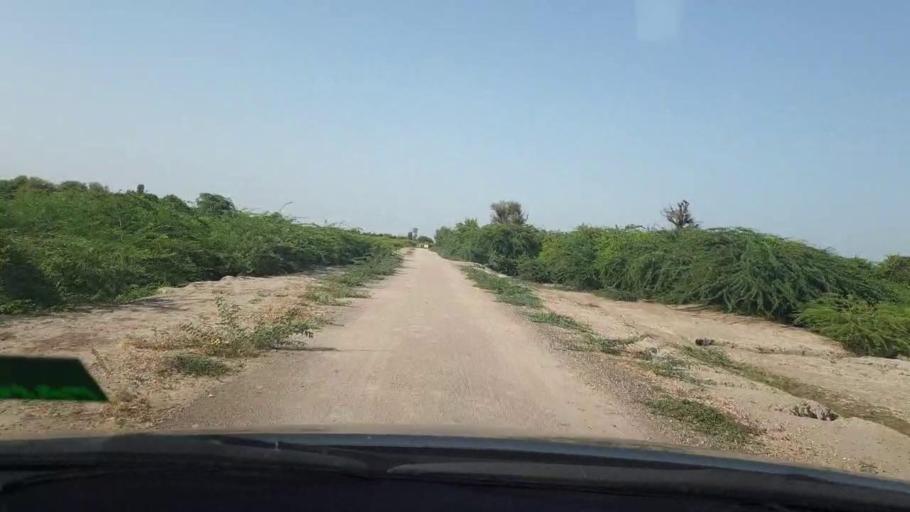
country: PK
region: Sindh
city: Naukot
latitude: 24.8700
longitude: 69.3171
